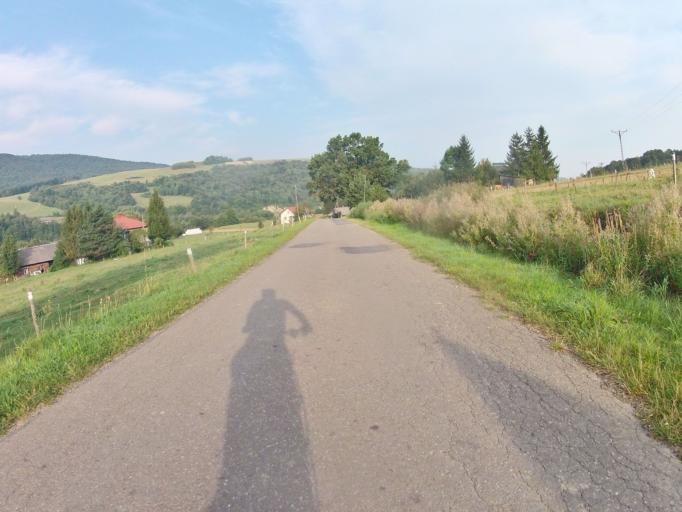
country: PL
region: Subcarpathian Voivodeship
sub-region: Powiat jasielski
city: Krempna
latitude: 49.5465
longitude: 21.5503
